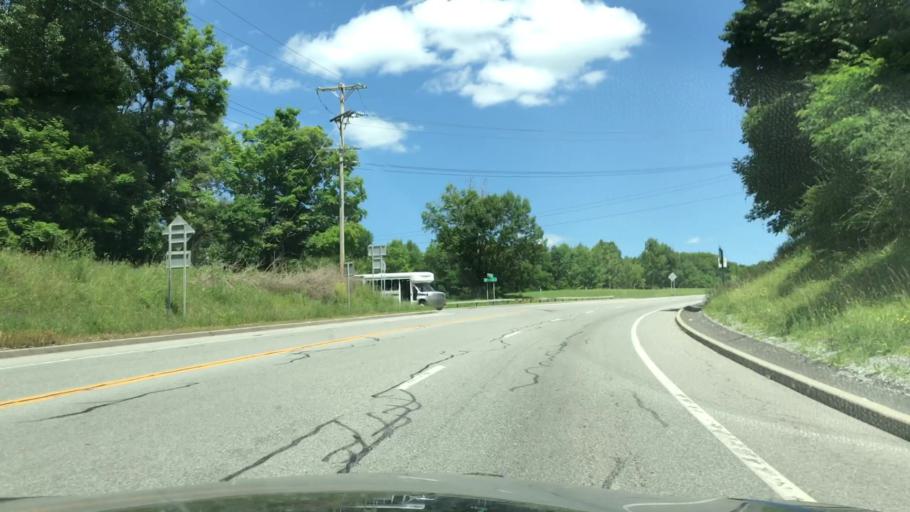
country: US
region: New York
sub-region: Wyoming County
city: Warsaw
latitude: 42.7466
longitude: -78.1252
